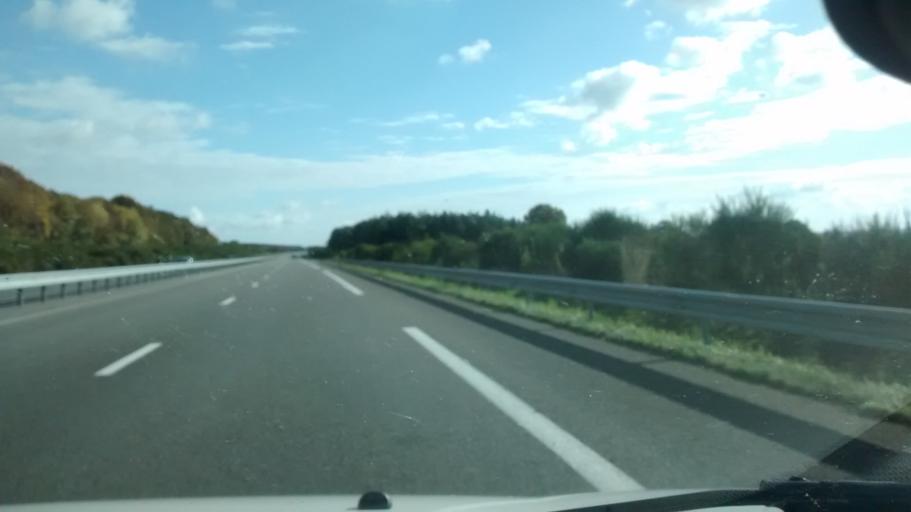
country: FR
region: Pays de la Loire
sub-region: Departement de Maine-et-Loire
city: Combree
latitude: 47.7232
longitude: -1.0492
